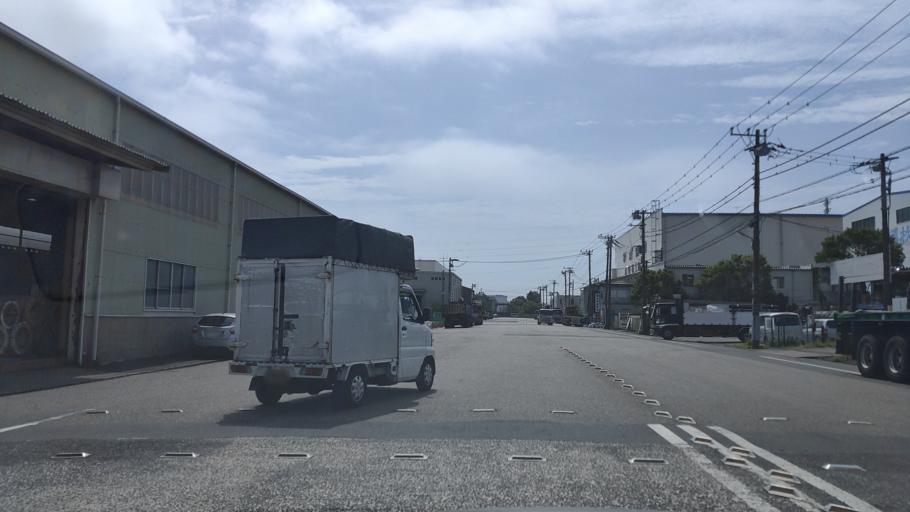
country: JP
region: Tokyo
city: Urayasu
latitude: 35.6344
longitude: 139.8979
